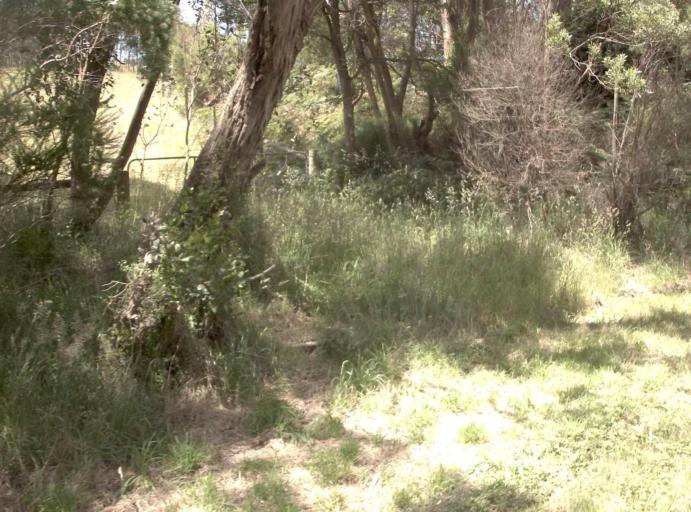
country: AU
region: Victoria
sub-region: Bass Coast
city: North Wonthaggi
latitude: -38.7281
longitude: 146.1216
